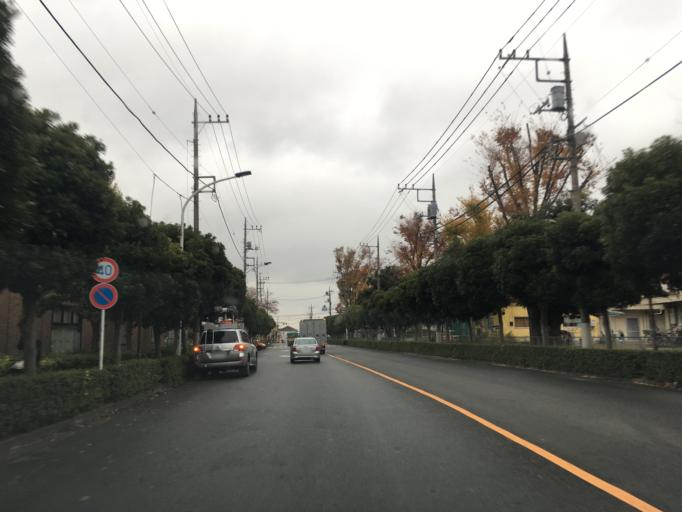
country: JP
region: Tokyo
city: Kokubunji
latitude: 35.6854
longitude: 139.4399
